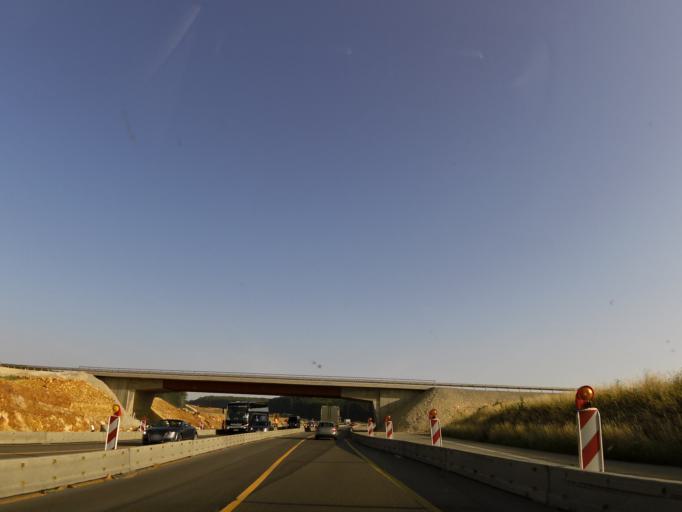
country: DE
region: Baden-Wuerttemberg
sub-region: Tuebingen Region
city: Nellingen
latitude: 48.5076
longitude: 9.8386
